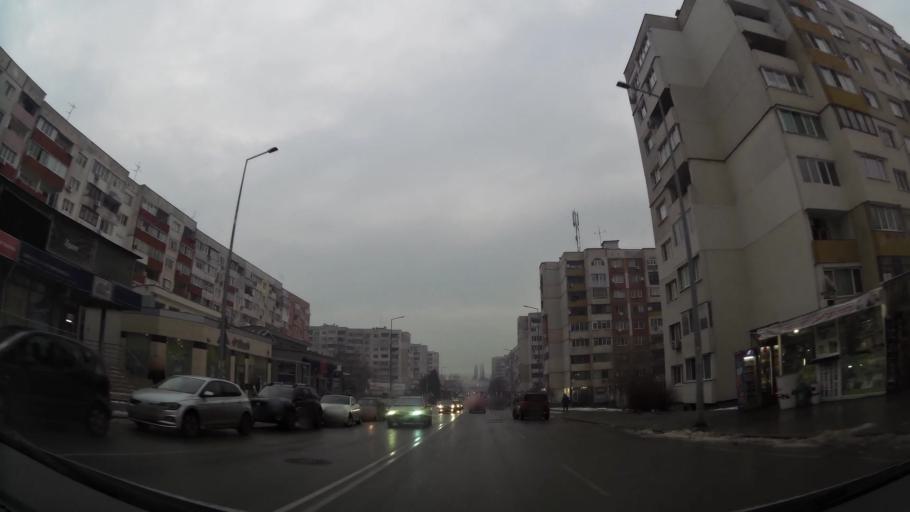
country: BG
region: Sofia-Capital
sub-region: Stolichna Obshtina
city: Sofia
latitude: 42.6870
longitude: 23.2554
